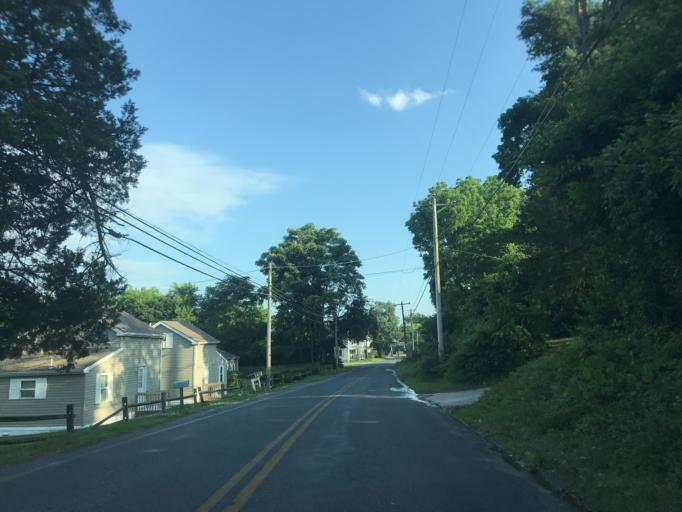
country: US
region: Maryland
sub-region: Caroline County
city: Federalsburg
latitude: 38.7022
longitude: -75.7759
